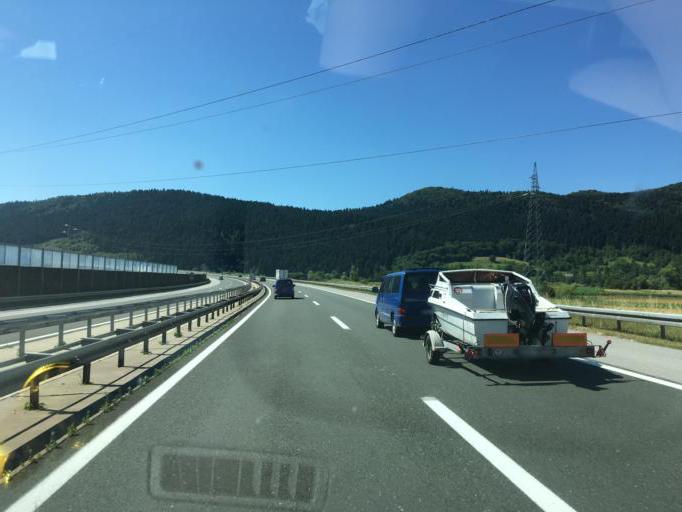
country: HR
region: Licko-Senjska
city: Otocac
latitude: 44.8689
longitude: 15.2075
